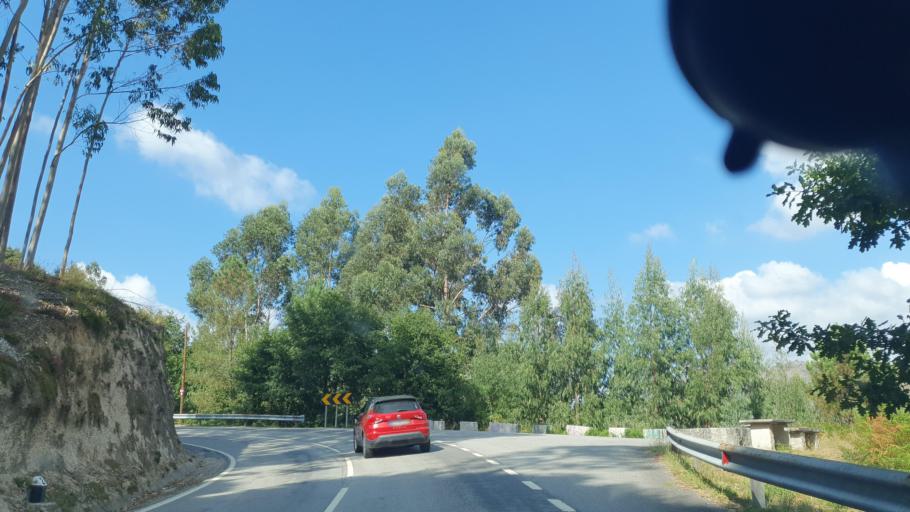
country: PT
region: Braga
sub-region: Terras de Bouro
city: Terras de Bouro
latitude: 41.7263
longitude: -8.2164
